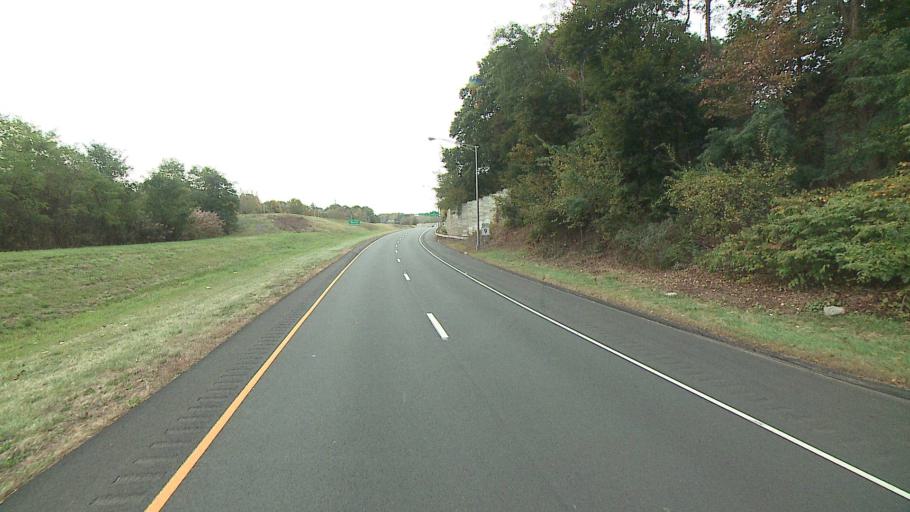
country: US
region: Connecticut
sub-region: Hartford County
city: West Hartford
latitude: 41.7227
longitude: -72.7717
